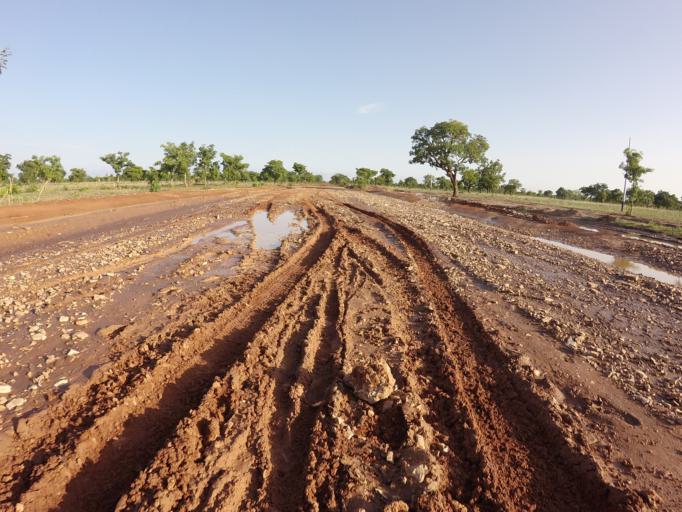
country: TG
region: Savanes
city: Sansanne-Mango
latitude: 10.3662
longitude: -0.0938
